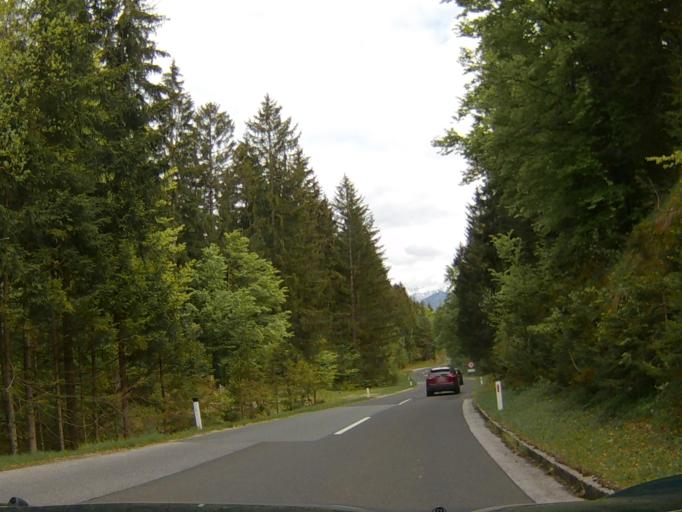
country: AT
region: Carinthia
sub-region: Villach Stadt
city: Villach
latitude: 46.5787
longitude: 13.7871
